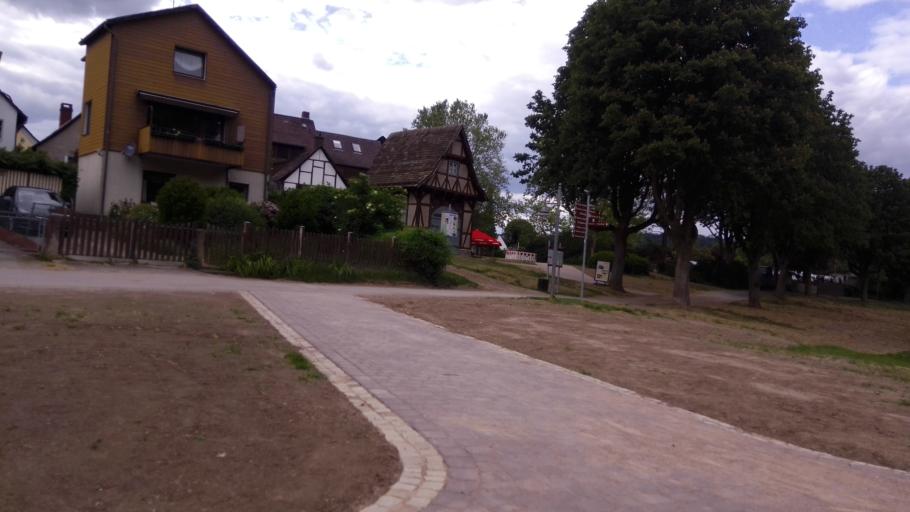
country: DE
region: Lower Saxony
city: Bodenwerder
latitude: 51.9790
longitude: 9.5188
